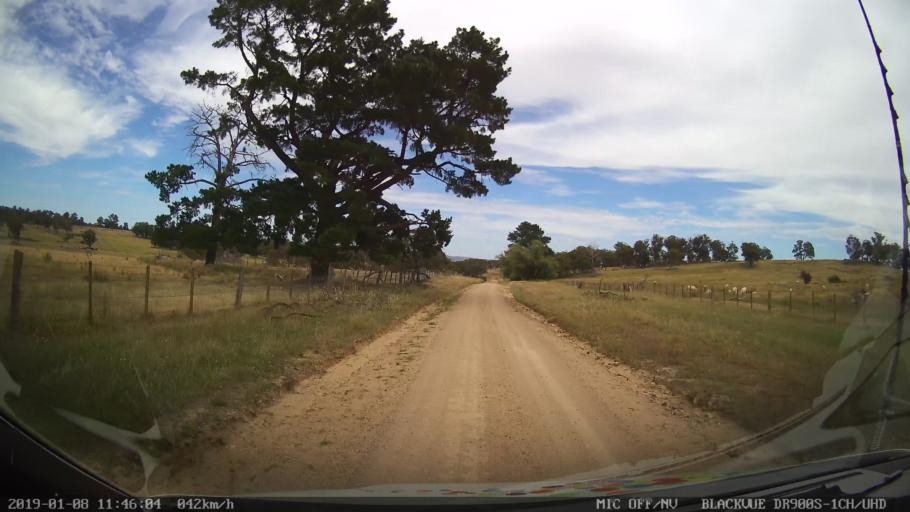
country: AU
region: New South Wales
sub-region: Armidale Dumaresq
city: Armidale
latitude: -30.3807
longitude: 151.5853
